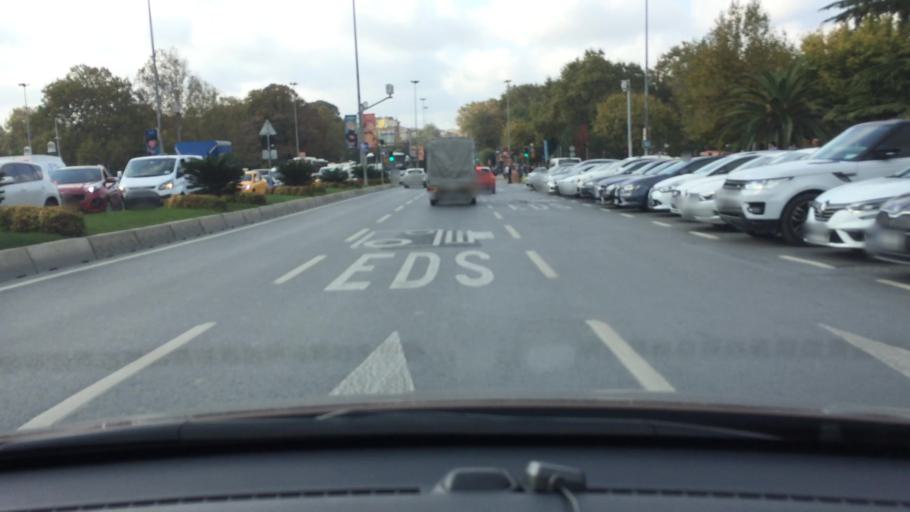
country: TR
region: Istanbul
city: Istanbul
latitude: 41.0141
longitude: 28.9554
